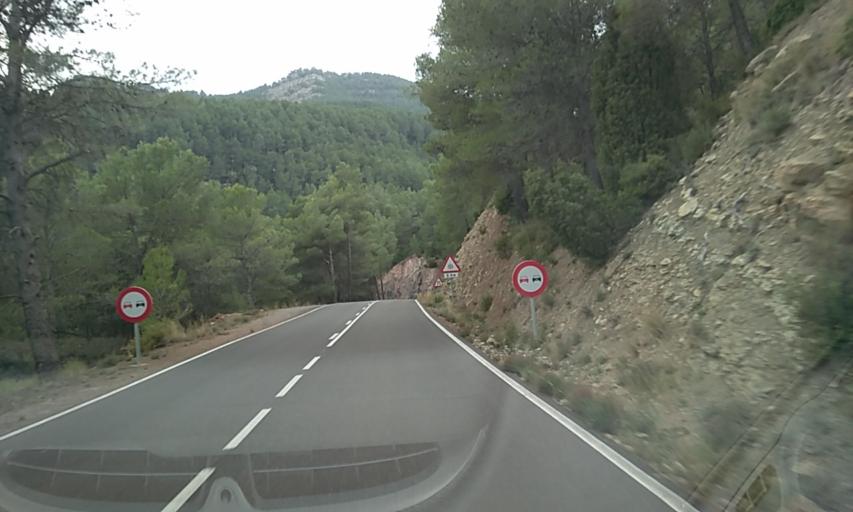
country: ES
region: Valencia
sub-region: Provincia de Castello
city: Puebla de Arenoso
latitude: 40.0949
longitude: -0.5738
